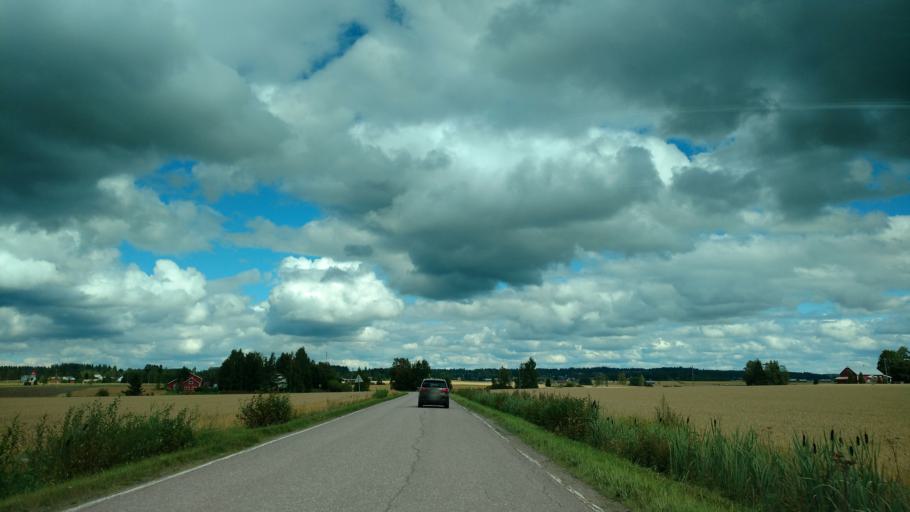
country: FI
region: Haeme
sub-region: Forssa
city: Ypaejae
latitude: 60.7816
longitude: 23.2687
